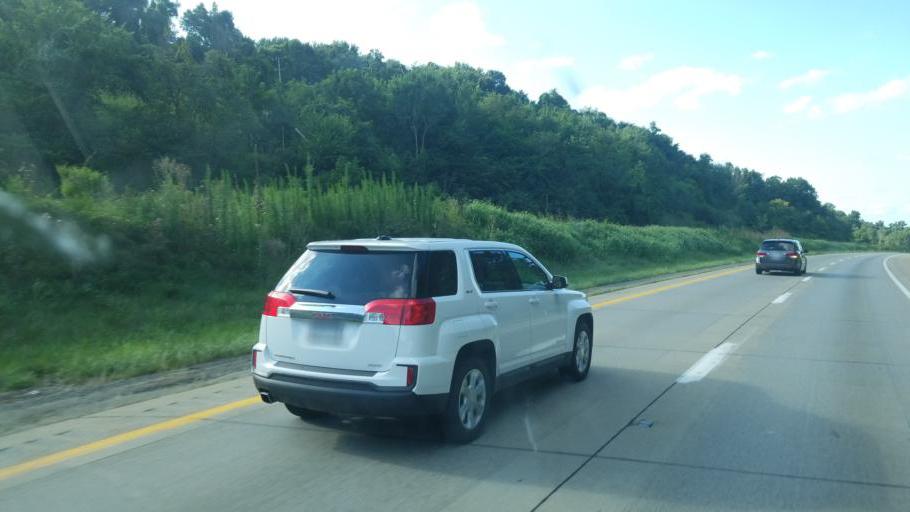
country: US
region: Pennsylvania
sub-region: Greene County
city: Waynesburg
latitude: 40.0007
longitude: -80.1891
